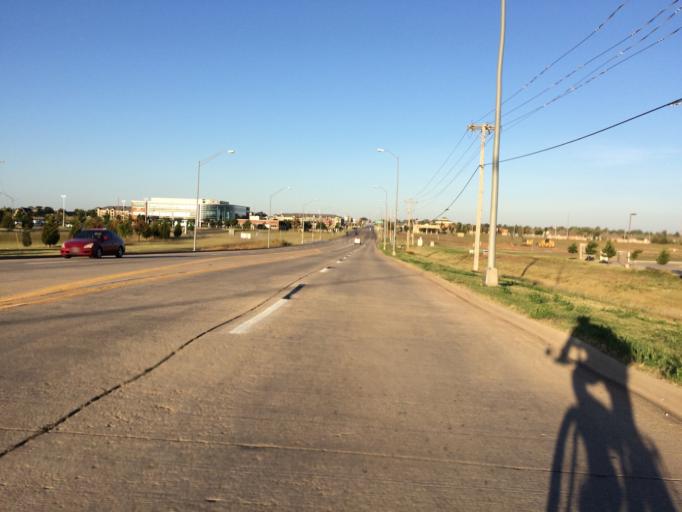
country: US
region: Oklahoma
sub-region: Cleveland County
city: Norman
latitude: 35.2620
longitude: -97.4877
